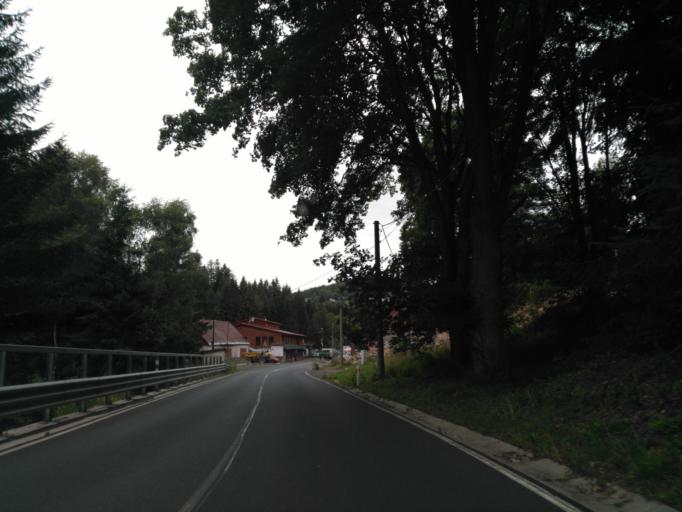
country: DE
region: Saxony
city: Johanngeorgenstadt
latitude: 50.4180
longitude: 12.7336
